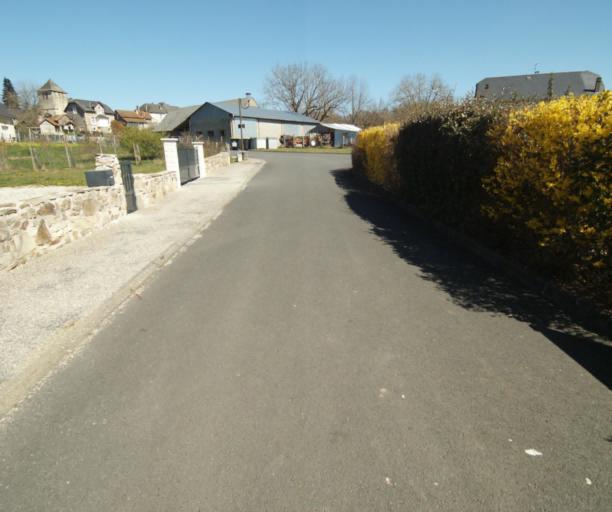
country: FR
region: Limousin
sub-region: Departement de la Correze
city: Saint-Clement
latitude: 45.3401
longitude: 1.6850
